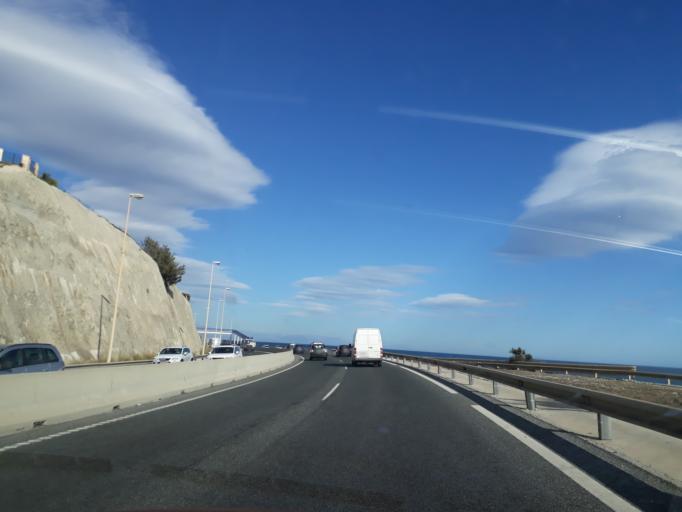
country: ES
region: Andalusia
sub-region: Provincia de Malaga
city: Fuengirola
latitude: 36.5071
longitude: -4.6396
